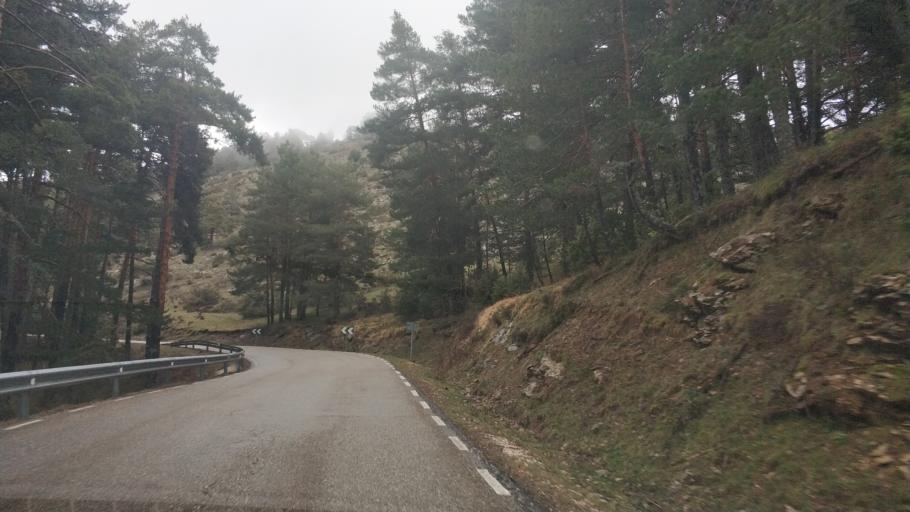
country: ES
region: Castille and Leon
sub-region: Provincia de Burgos
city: Neila
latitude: 42.0379
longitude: -3.0046
